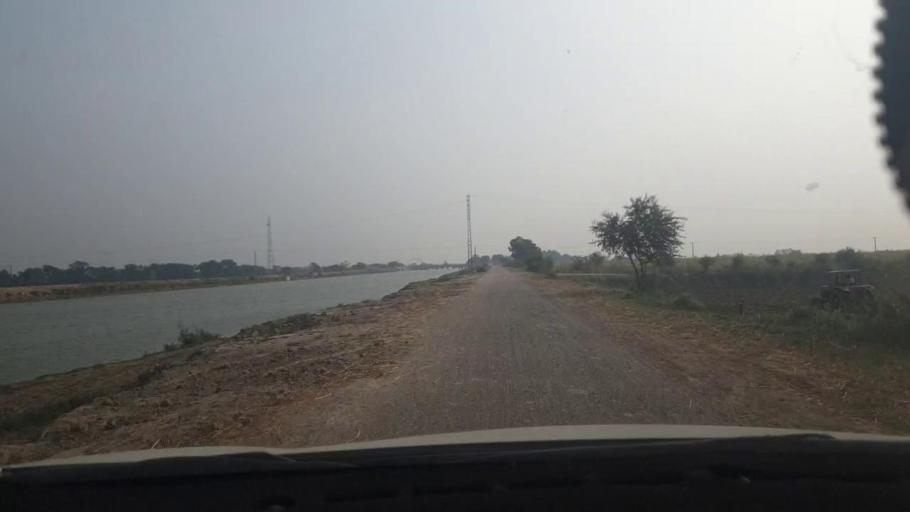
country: PK
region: Sindh
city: Tando Muhammad Khan
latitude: 24.9645
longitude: 68.4953
